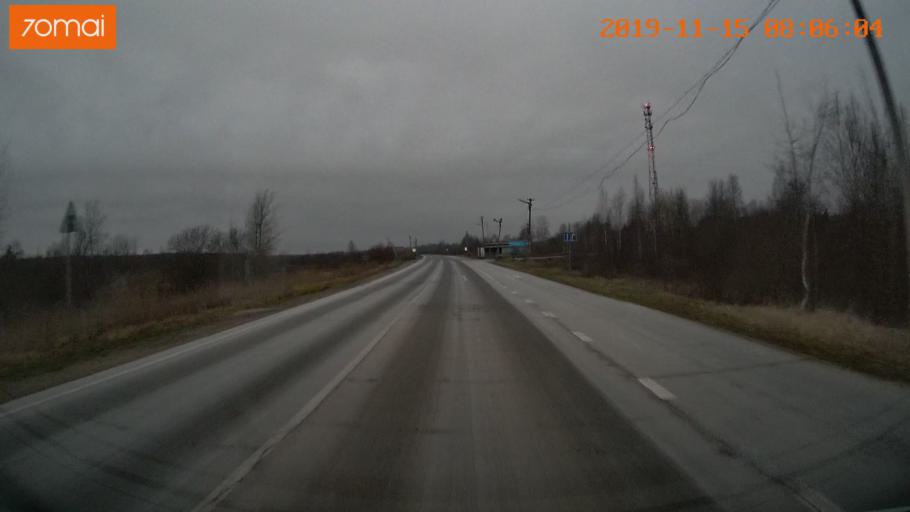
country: RU
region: Vologda
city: Cherepovets
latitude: 59.0204
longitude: 38.0456
